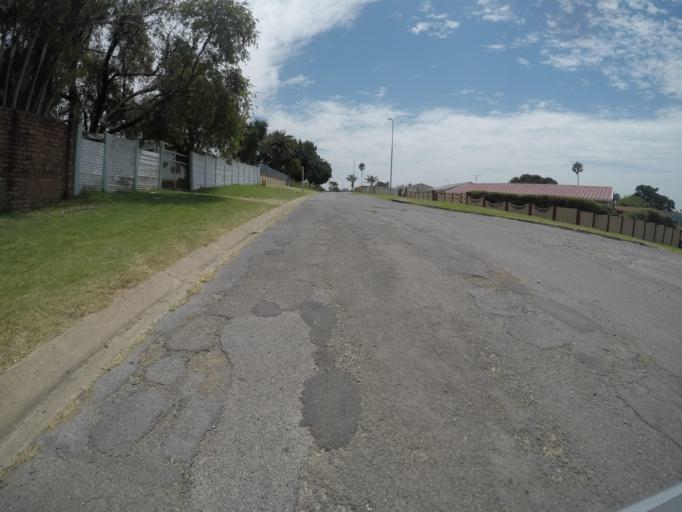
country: ZA
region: Eastern Cape
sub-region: Buffalo City Metropolitan Municipality
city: East London
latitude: -32.9778
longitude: 27.8636
